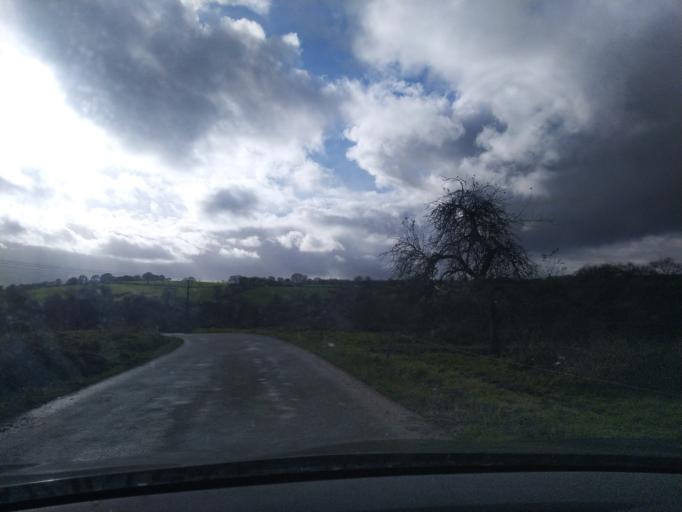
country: FR
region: Brittany
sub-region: Departement du Finistere
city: Guerlesquin
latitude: 48.4265
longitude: -3.6159
